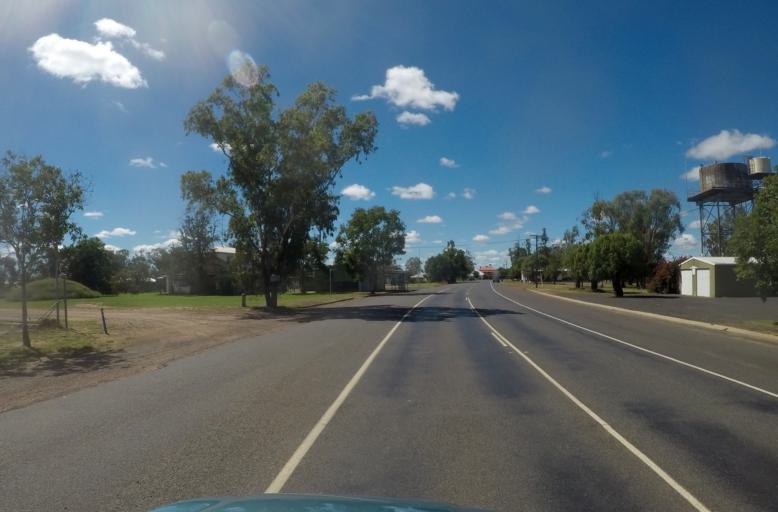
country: AU
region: Queensland
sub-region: Western Downs
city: Westcourt
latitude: -26.6436
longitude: 149.7618
